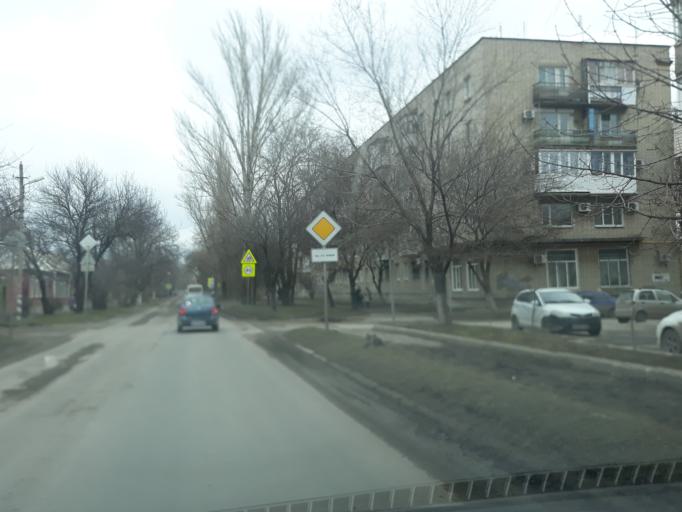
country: RU
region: Rostov
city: Taganrog
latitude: 47.2652
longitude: 38.9177
